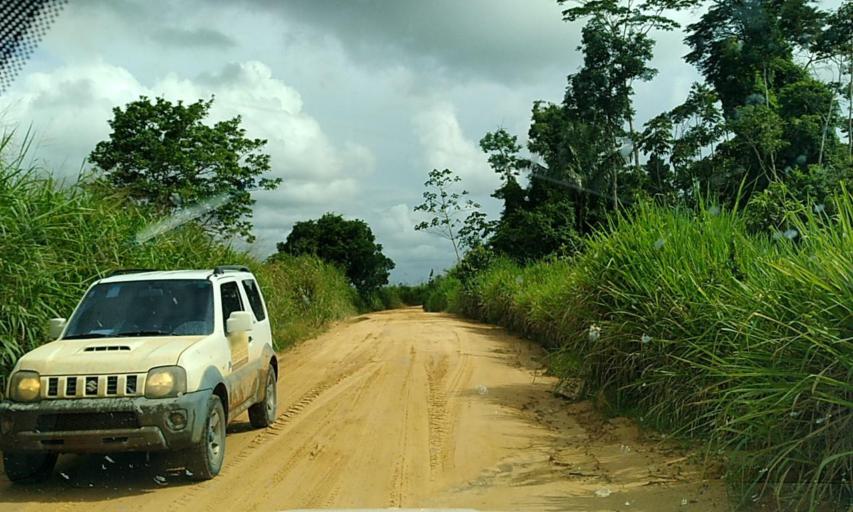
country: BR
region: Para
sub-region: Altamira
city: Altamira
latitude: -3.2378
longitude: -52.6953
